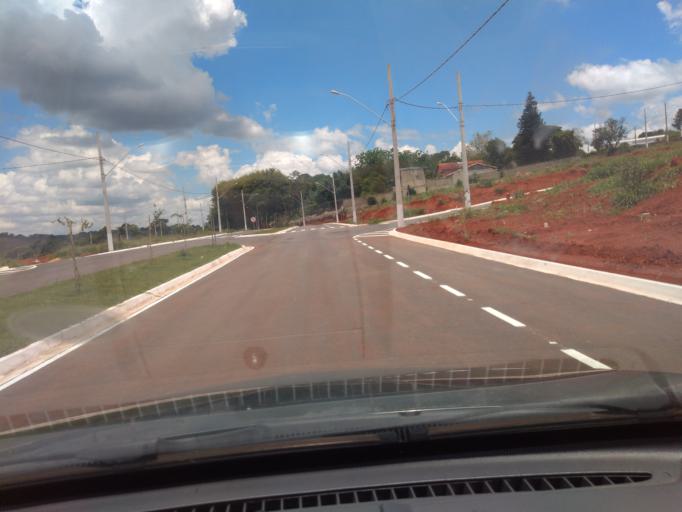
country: BR
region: Minas Gerais
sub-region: Tres Coracoes
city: Tres Coracoes
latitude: -21.6645
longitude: -45.2778
